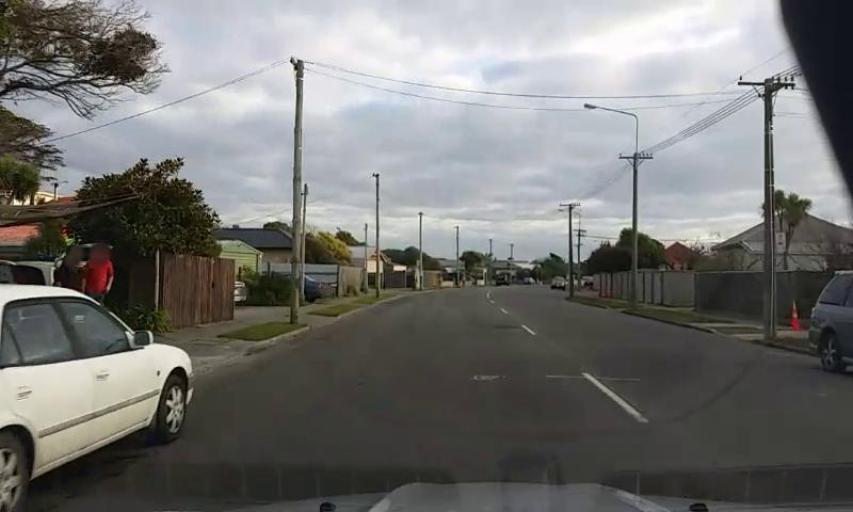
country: NZ
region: Canterbury
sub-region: Christchurch City
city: Christchurch
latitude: -43.5171
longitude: 172.7299
